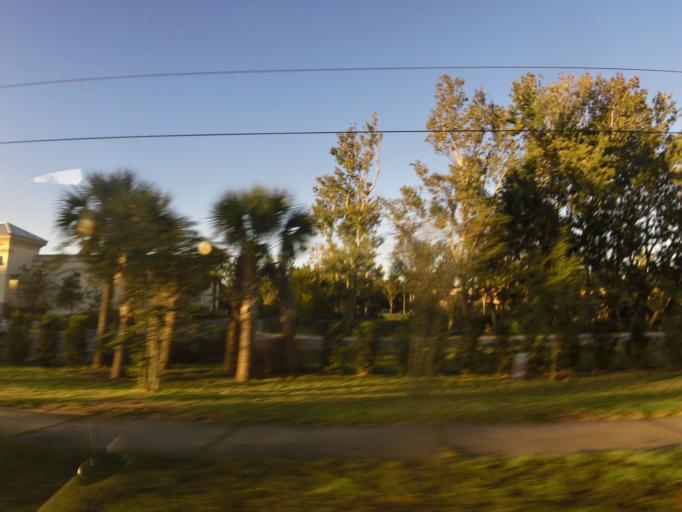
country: US
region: Florida
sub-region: Flagler County
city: Palm Coast
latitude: 29.5574
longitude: -81.2158
